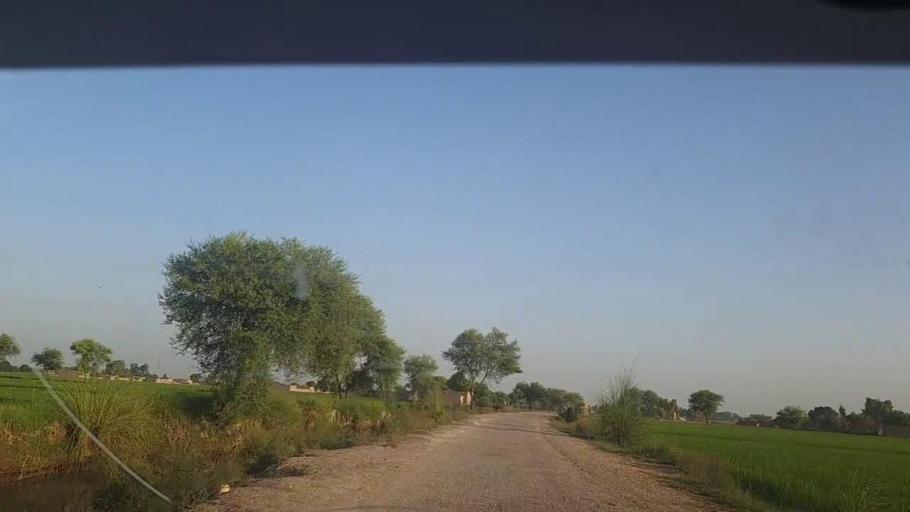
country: PK
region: Sindh
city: Thul
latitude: 28.1219
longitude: 68.8949
